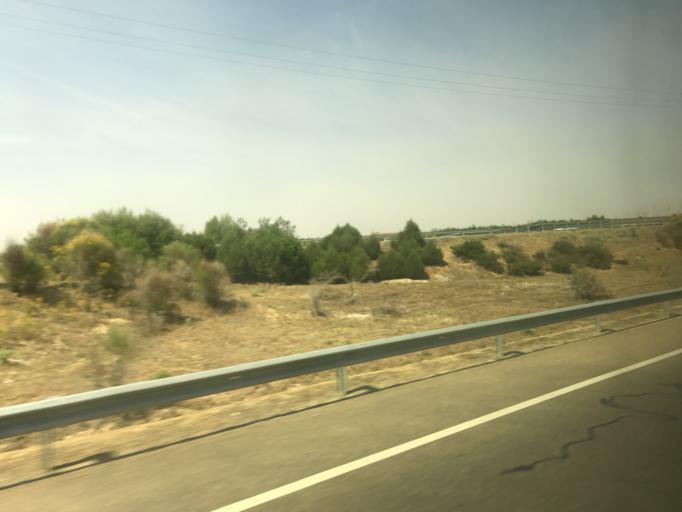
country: ES
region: Castille and Leon
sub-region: Provincia de Palencia
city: Villalobon
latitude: 42.0198
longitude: -4.5077
